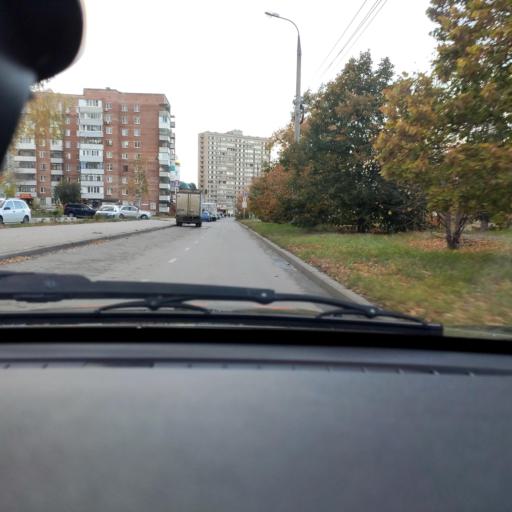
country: RU
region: Samara
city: Zhigulevsk
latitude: 53.4757
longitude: 49.5267
